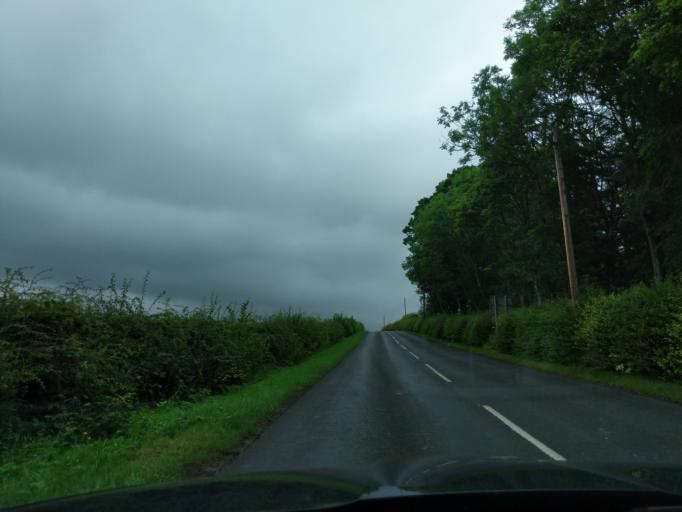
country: GB
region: England
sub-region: Northumberland
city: Ford
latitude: 55.6316
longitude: -2.0979
